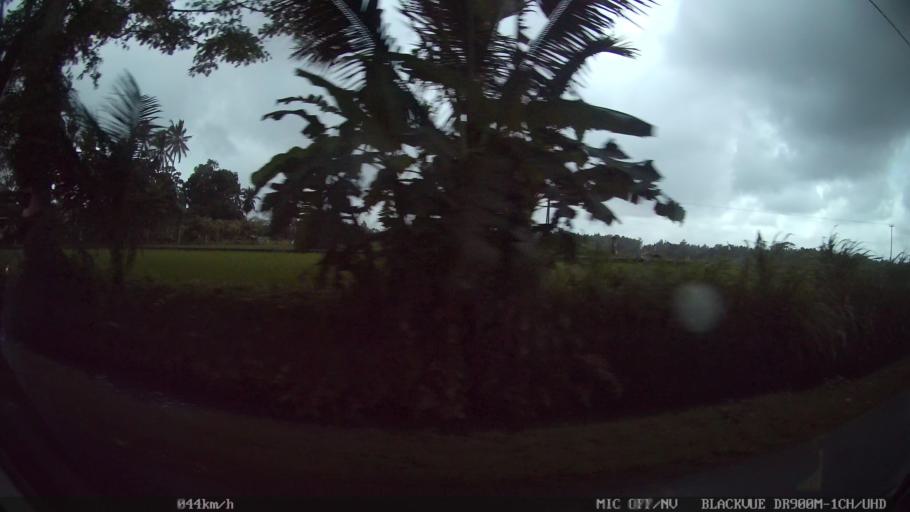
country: ID
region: Bali
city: Banjar Badung Tengah
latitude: -8.5121
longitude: 115.1990
